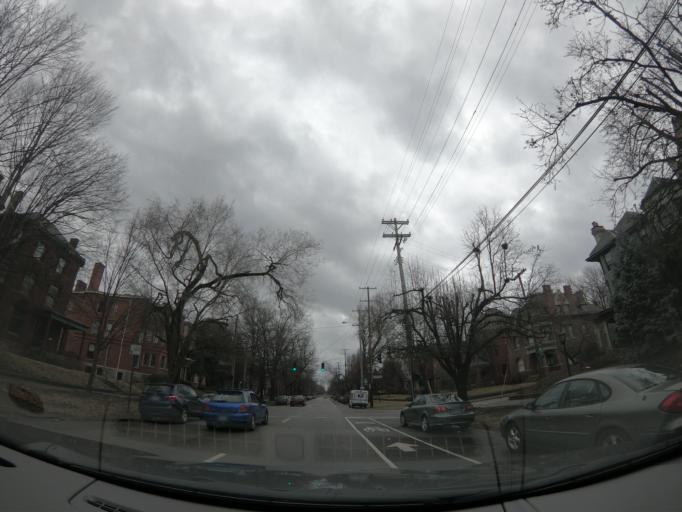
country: US
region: Kentucky
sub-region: Jefferson County
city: Louisville
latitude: 38.2292
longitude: -85.7597
